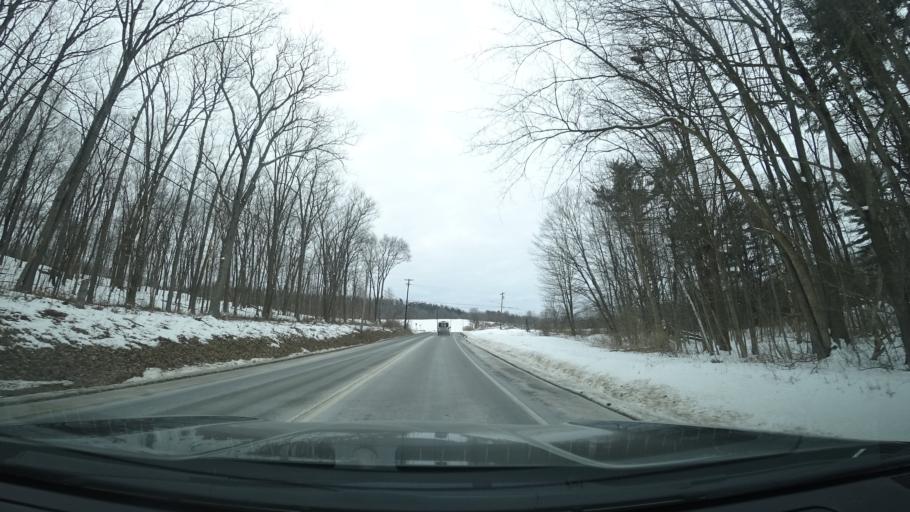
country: US
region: New York
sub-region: Washington County
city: Fort Edward
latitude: 43.2075
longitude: -73.4866
